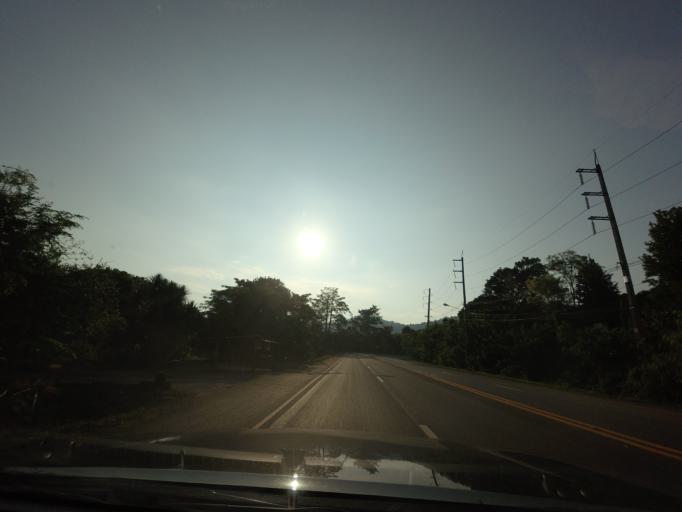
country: TH
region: Loei
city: Dan Sai
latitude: 17.2104
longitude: 101.1545
